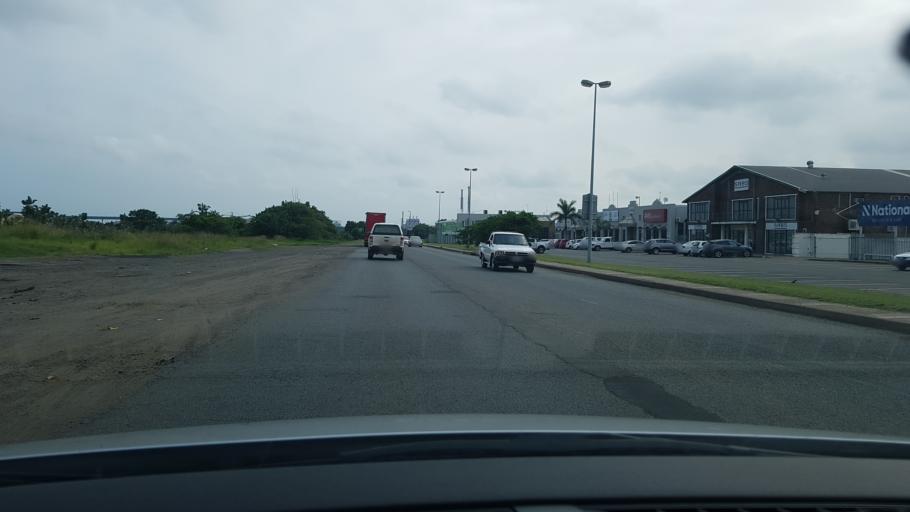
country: ZA
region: KwaZulu-Natal
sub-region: uThungulu District Municipality
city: Richards Bay
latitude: -28.7596
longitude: 32.0438
